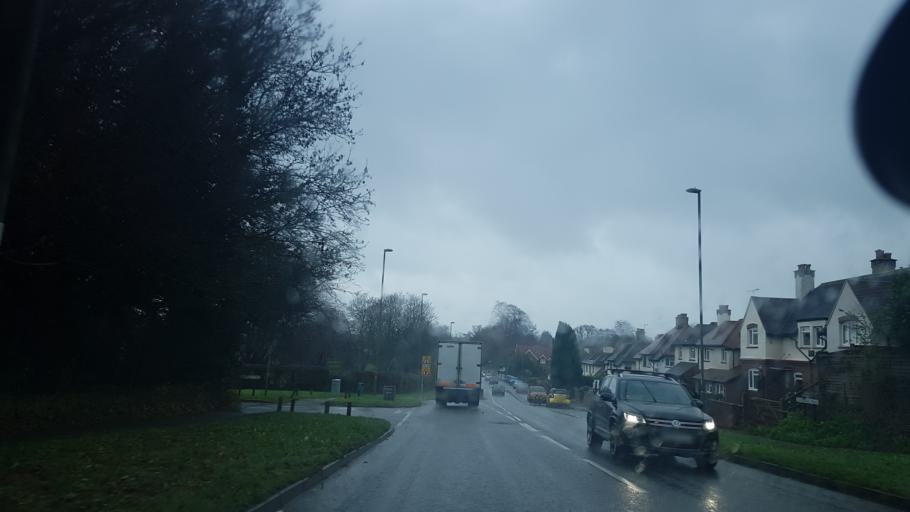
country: GB
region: England
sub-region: Surrey
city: Great Bookham
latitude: 51.2683
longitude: -0.3968
